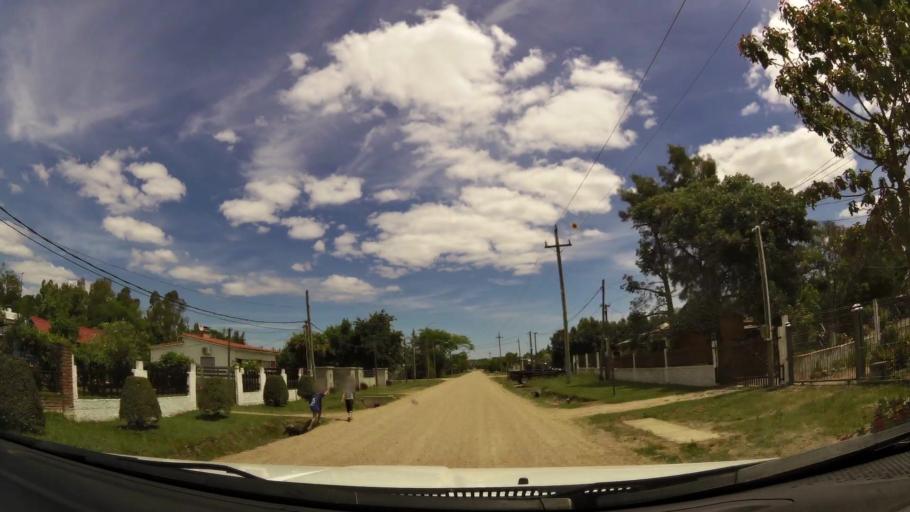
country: UY
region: San Jose
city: Delta del Tigre
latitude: -34.7401
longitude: -56.4413
